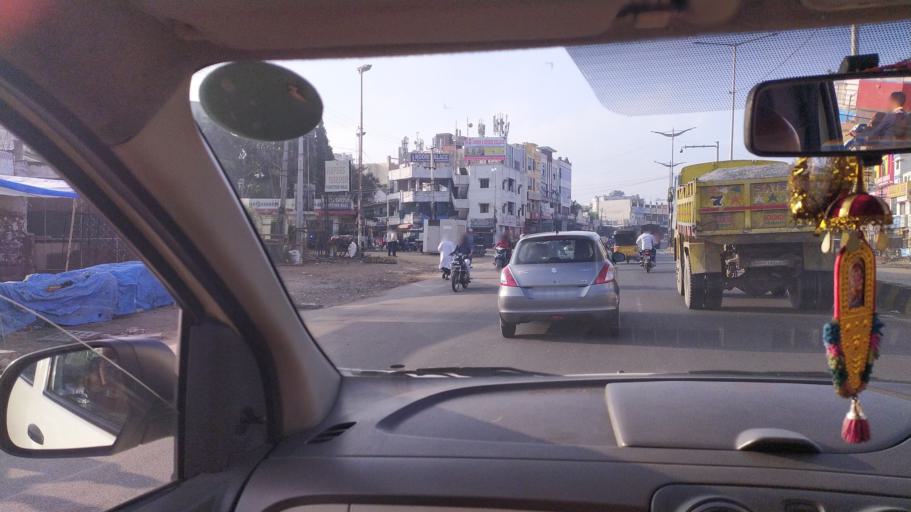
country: IN
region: Telangana
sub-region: Rangareddi
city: Balapur
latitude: 17.3173
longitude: 78.4666
